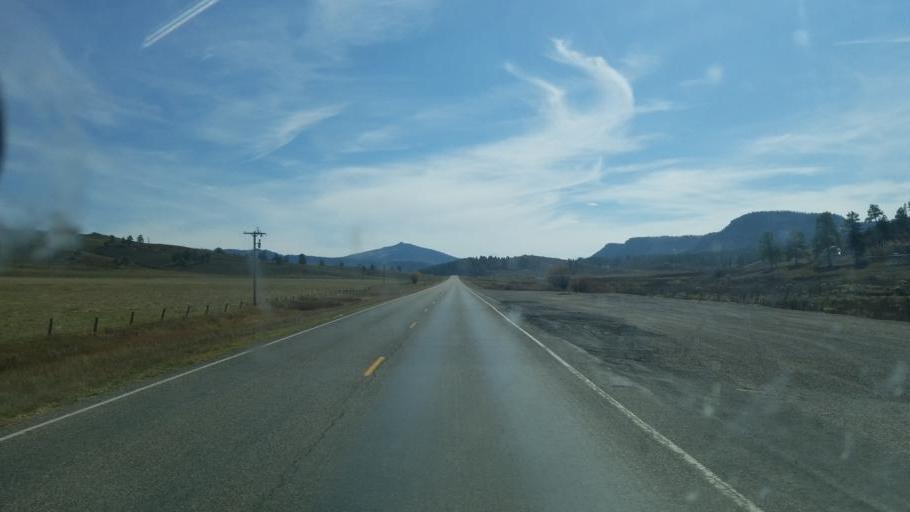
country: US
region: New Mexico
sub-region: Rio Arriba County
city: Dulce
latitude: 37.0297
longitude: -106.8272
